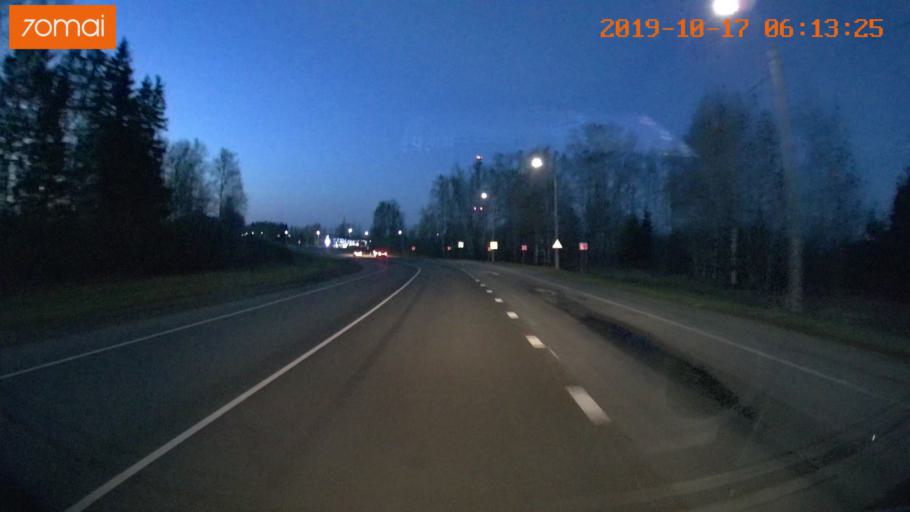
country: RU
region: Ivanovo
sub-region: Gorod Ivanovo
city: Ivanovo
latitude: 56.8986
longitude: 40.9358
